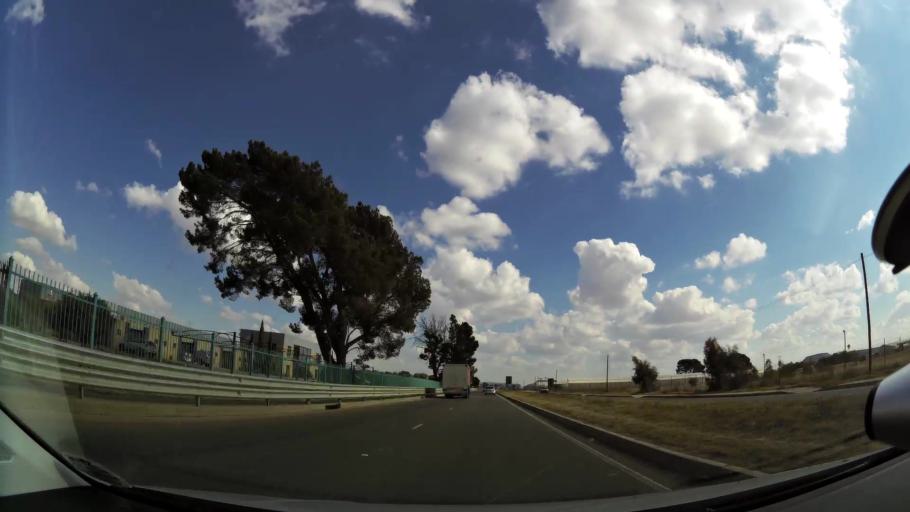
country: ZA
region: Orange Free State
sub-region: Mangaung Metropolitan Municipality
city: Bloemfontein
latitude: -29.1293
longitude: 26.1536
